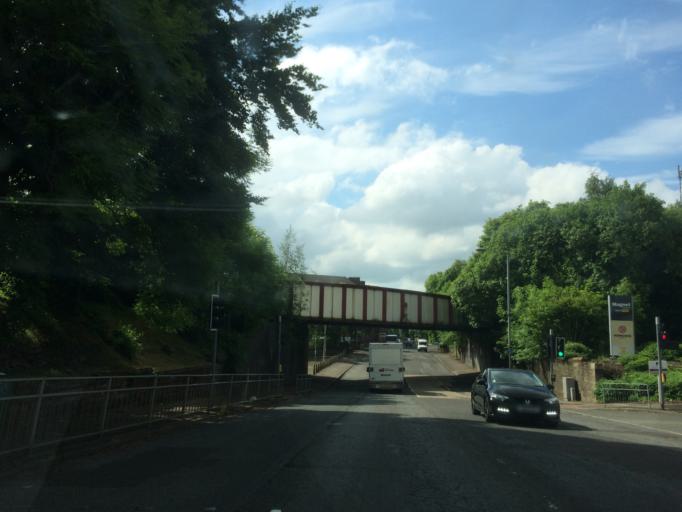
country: GB
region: Scotland
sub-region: East Renfrewshire
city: Giffnock
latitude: 55.8297
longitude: -4.2958
